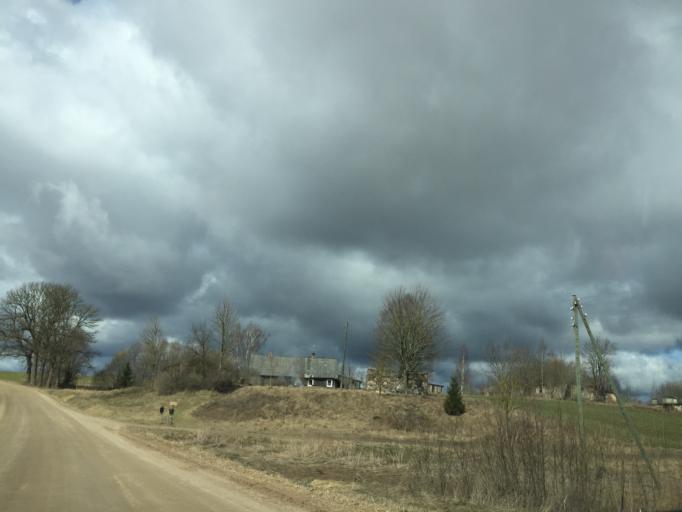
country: LV
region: Akniste
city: Akniste
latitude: 56.1050
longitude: 25.9544
